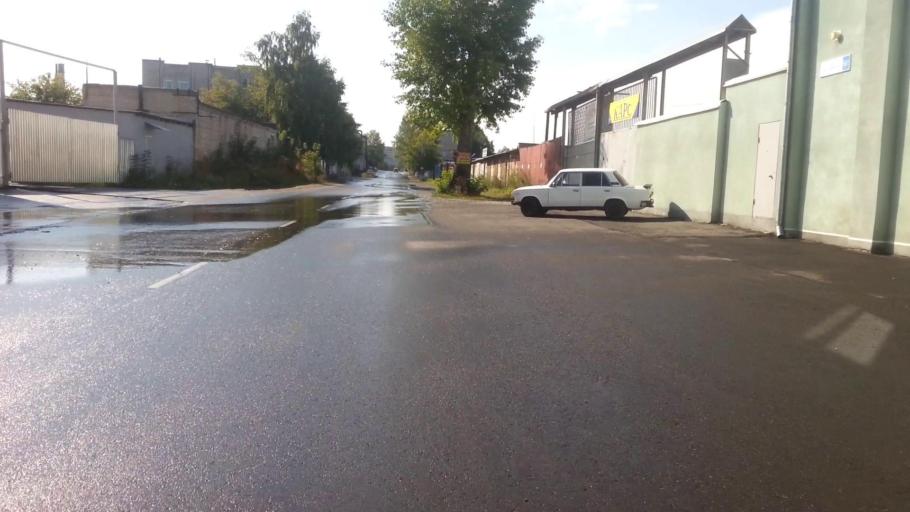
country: RU
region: Altai Krai
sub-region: Gorod Barnaulskiy
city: Barnaul
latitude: 53.3446
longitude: 83.7212
